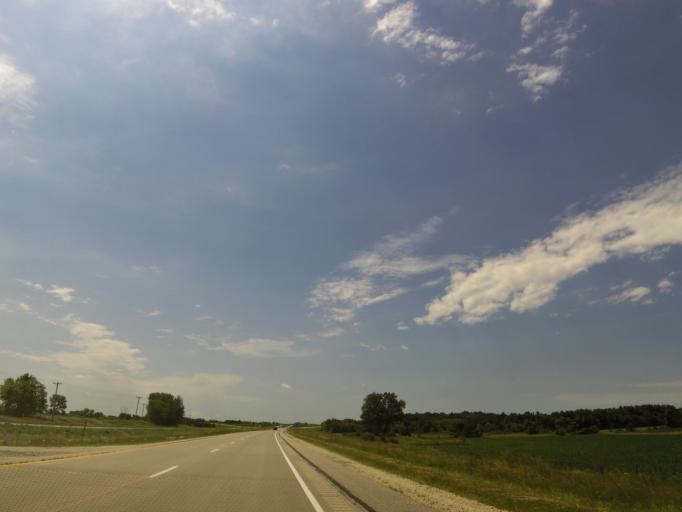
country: US
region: Iowa
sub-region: Bremer County
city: Denver
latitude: 42.7247
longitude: -92.3373
